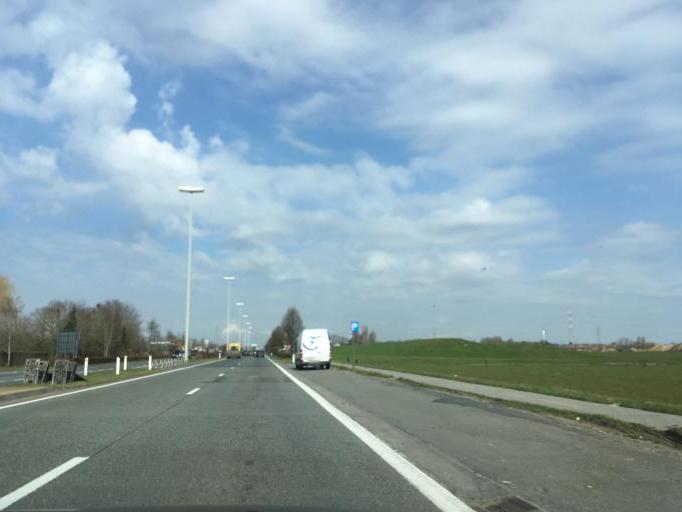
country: BE
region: Flanders
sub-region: Provincie West-Vlaanderen
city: Deerlijk
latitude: 50.8550
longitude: 3.3334
